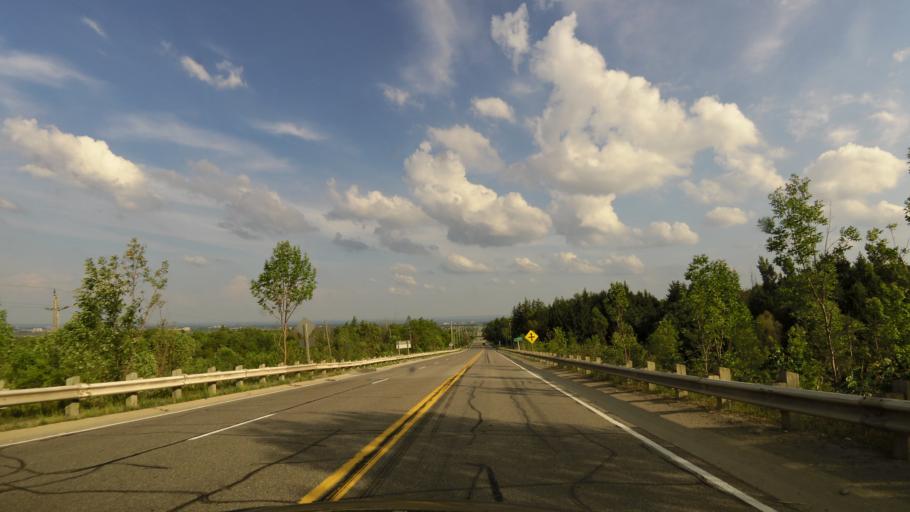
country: CA
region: Ontario
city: Burlington
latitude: 43.3927
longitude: -79.8600
